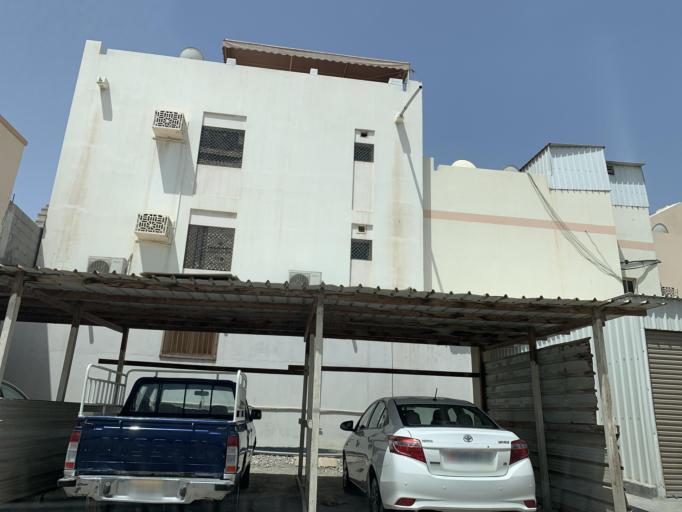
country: BH
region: Northern
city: Sitrah
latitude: 26.1426
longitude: 50.6104
